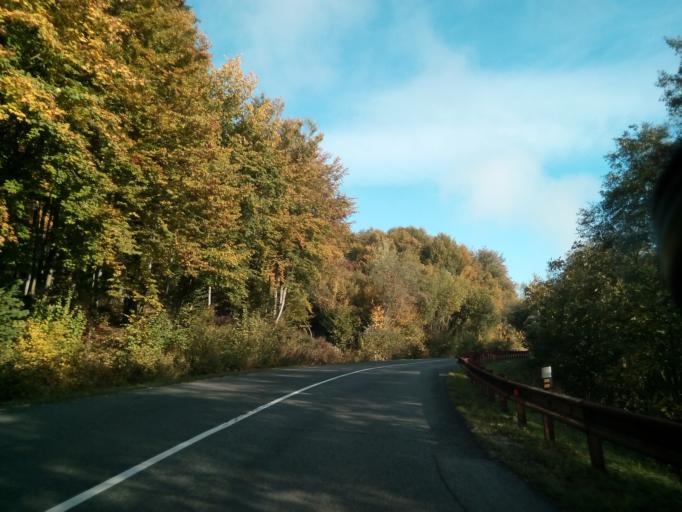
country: SK
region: Kosicky
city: Gelnica
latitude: 48.8414
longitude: 21.0358
